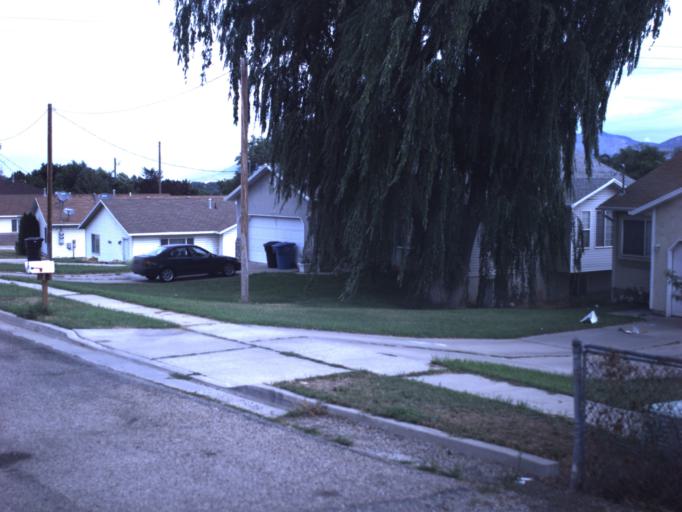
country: US
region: Utah
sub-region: Weber County
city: Riverdale
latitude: 41.1595
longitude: -112.0064
